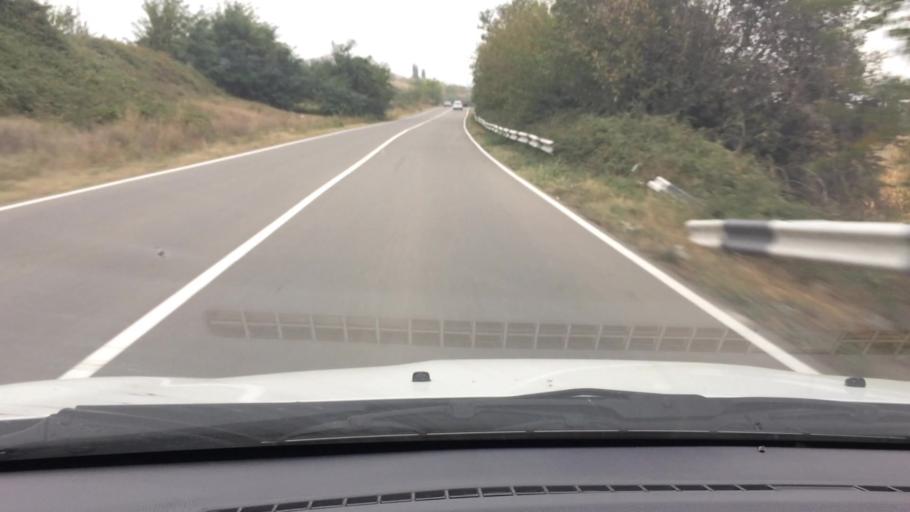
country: AM
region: Tavush
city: Bagratashen
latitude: 41.2699
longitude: 44.7909
